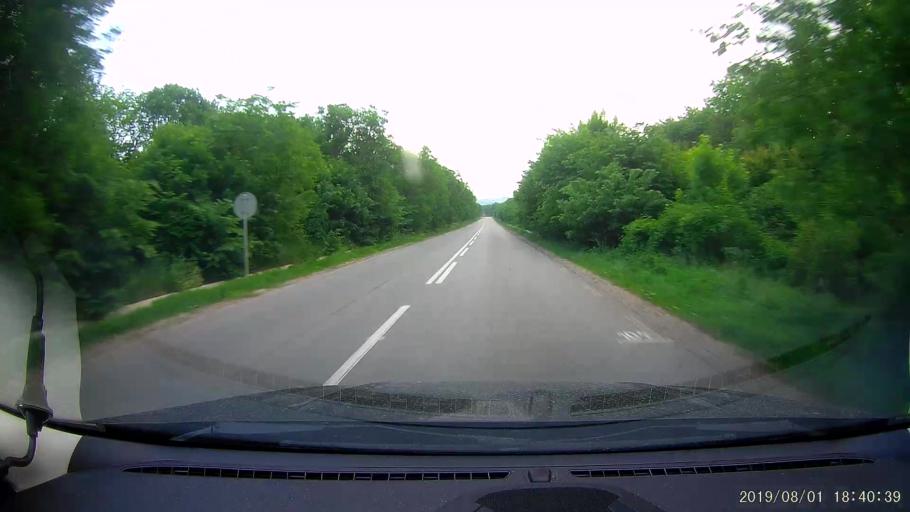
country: BG
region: Shumen
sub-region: Obshtina Khitrino
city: Gara Khitrino
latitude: 43.3623
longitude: 26.9202
